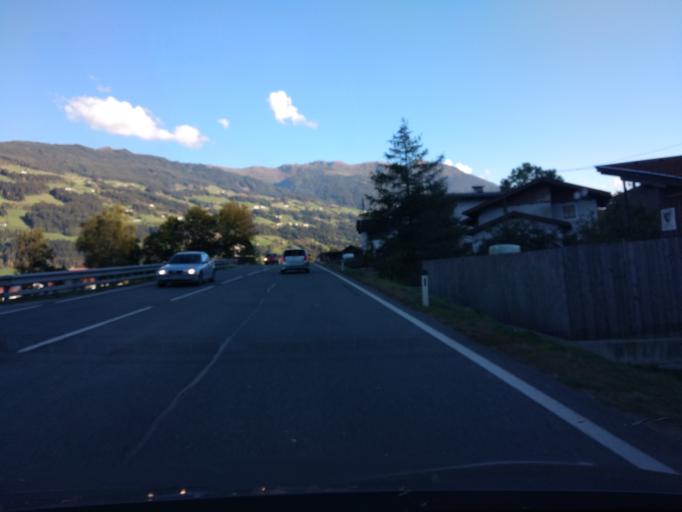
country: AT
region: Tyrol
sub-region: Politischer Bezirk Schwaz
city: Schlitters
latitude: 47.3789
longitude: 11.8399
